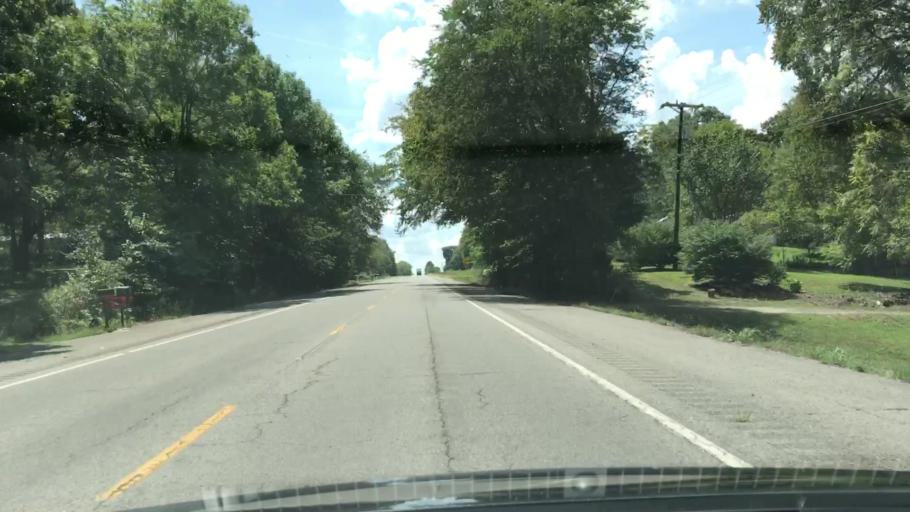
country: US
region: Tennessee
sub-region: Sumner County
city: White House
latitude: 36.5220
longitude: -86.6387
